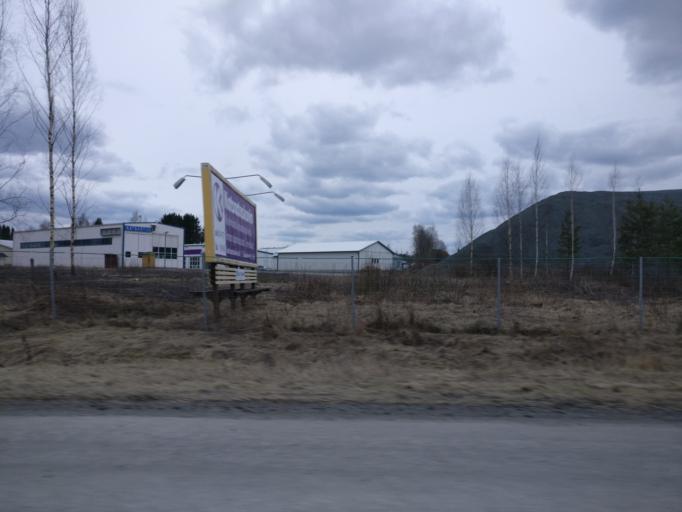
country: FI
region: Haeme
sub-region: Haemeenlinna
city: Haemeenlinna
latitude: 61.0161
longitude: 24.4105
